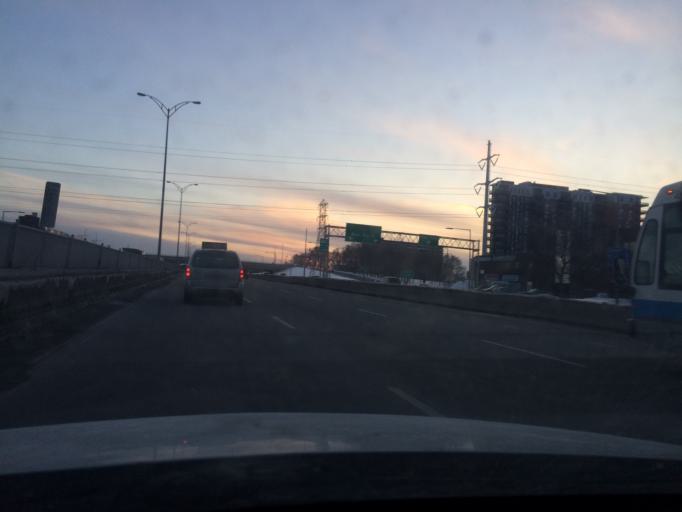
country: CA
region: Quebec
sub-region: Montreal
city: Saint-Leonard
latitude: 45.5786
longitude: -73.5923
